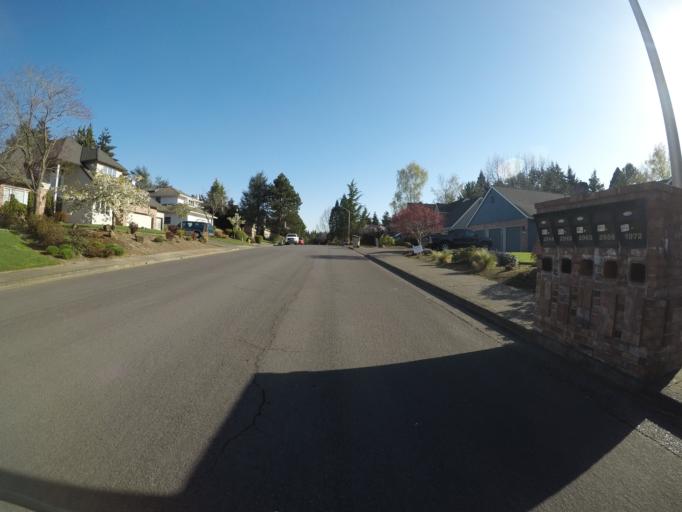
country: US
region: Oregon
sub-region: Washington County
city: Cedar Mill
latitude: 45.5411
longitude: -122.8149
